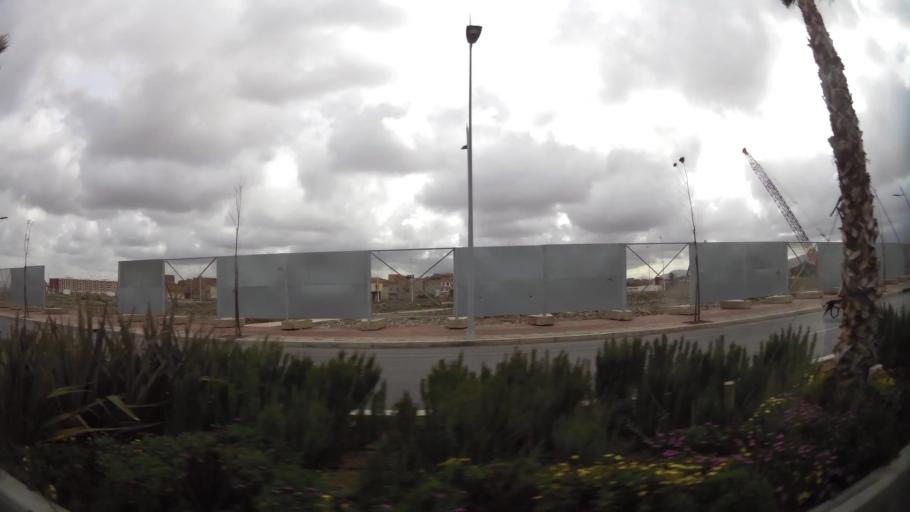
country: MA
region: Oriental
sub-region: Nador
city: Nador
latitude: 35.1609
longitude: -2.9070
